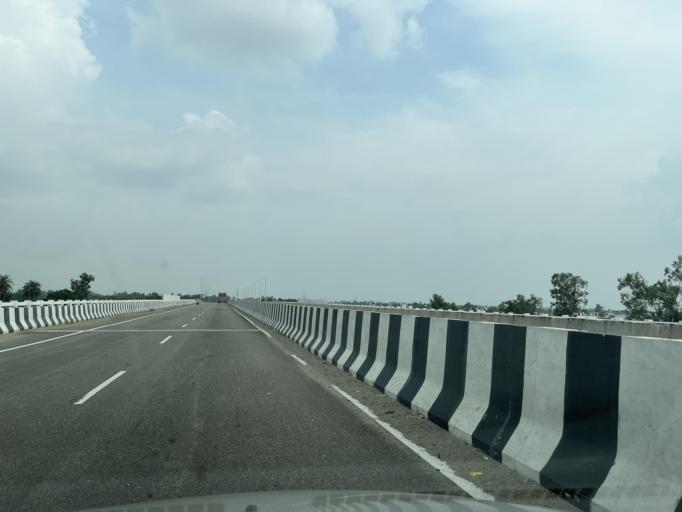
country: IN
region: Uttarakhand
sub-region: Udham Singh Nagar
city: Kashipur
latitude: 29.1739
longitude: 78.9459
